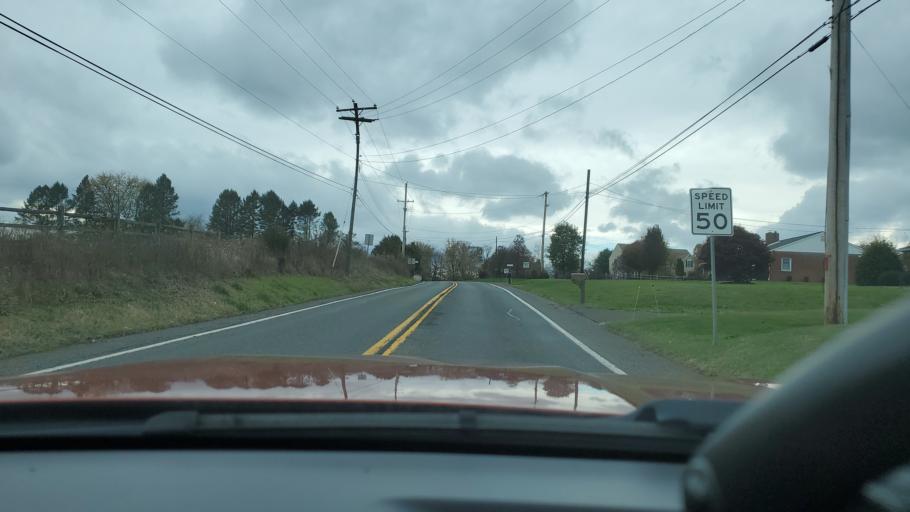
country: US
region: Pennsylvania
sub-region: Montgomery County
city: Spring Mount
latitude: 40.2842
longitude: -75.5050
